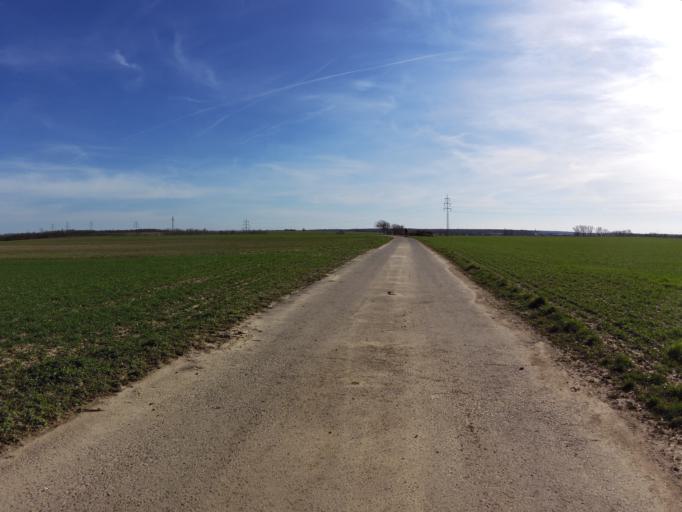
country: DE
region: Bavaria
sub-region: Regierungsbezirk Unterfranken
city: Biebelried
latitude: 49.7486
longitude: 10.0964
